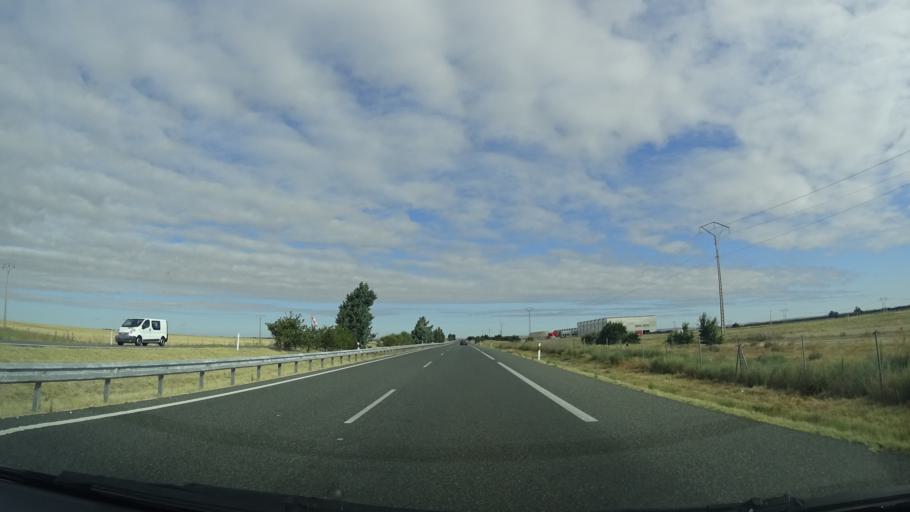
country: ES
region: Castille and Leon
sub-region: Provincia de Valladolid
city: San Vicente del Palacio
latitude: 41.2524
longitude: -4.8719
